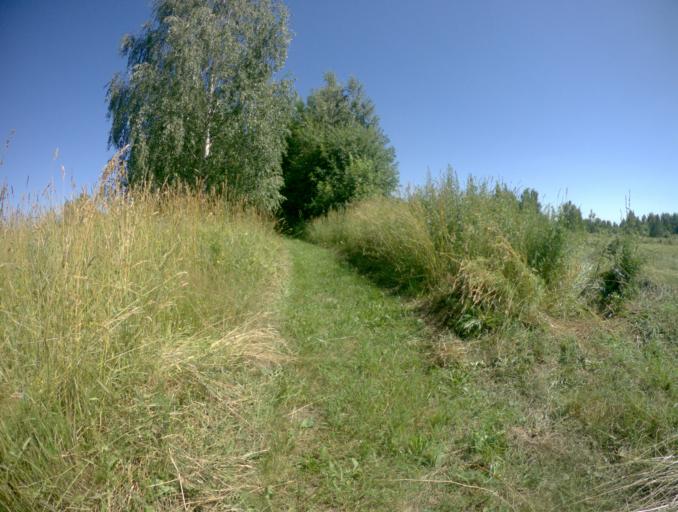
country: RU
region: Nizjnij Novgorod
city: Gorbatov
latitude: 56.0777
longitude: 43.0980
